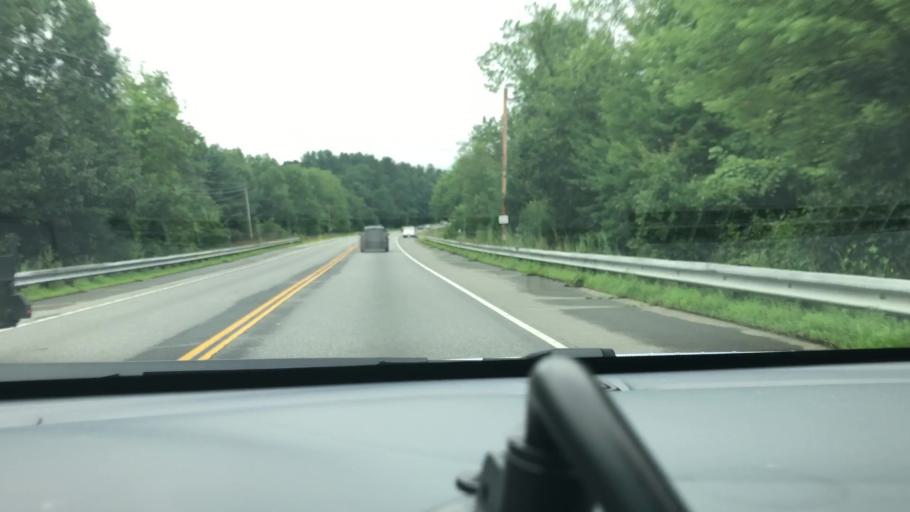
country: US
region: New Hampshire
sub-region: Hillsborough County
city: Pinardville
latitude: 42.9778
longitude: -71.5177
